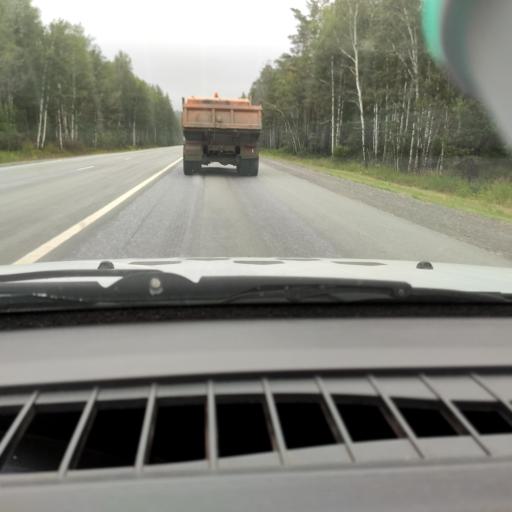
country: RU
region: Chelyabinsk
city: Syrostan
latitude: 55.0167
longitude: 59.7835
